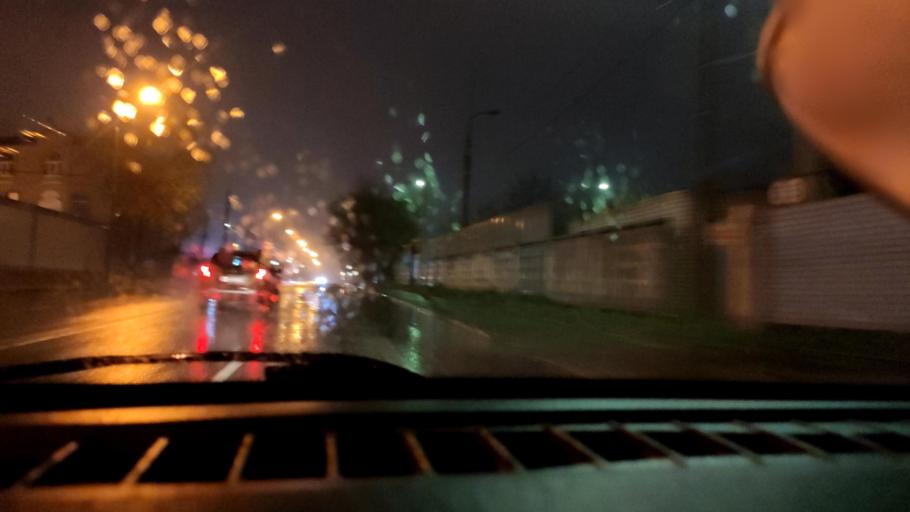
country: RU
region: Samara
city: Samara
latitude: 53.1854
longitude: 50.1470
